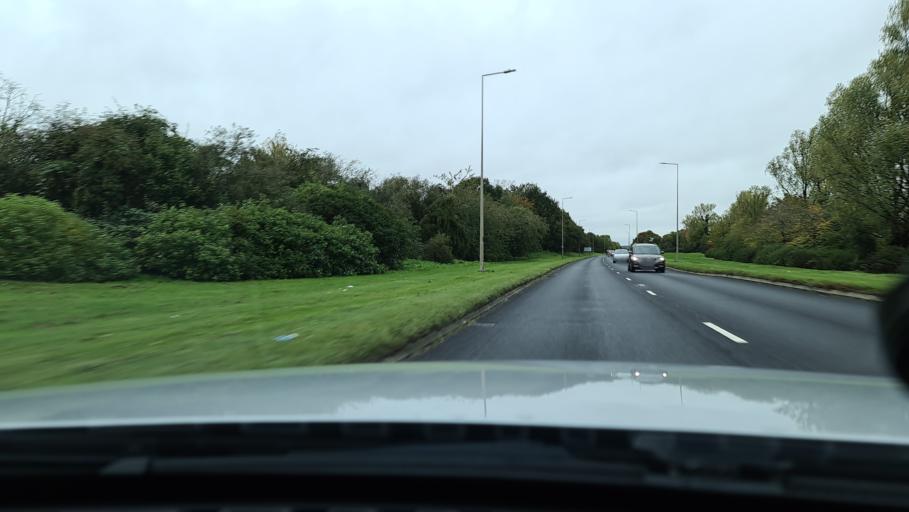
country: GB
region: England
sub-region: Milton Keynes
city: Bradwell
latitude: 52.0545
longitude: -0.8182
